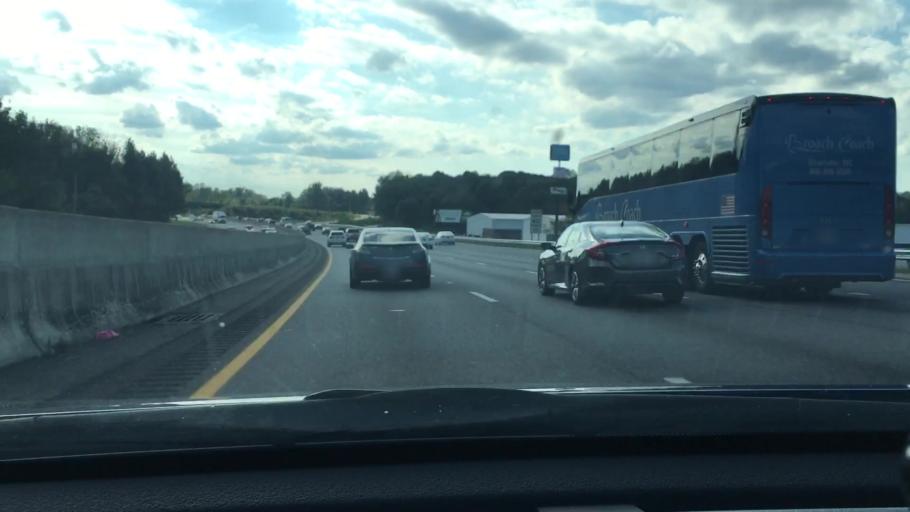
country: US
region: South Carolina
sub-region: Richland County
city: Columbia
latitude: 34.0657
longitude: -81.0411
